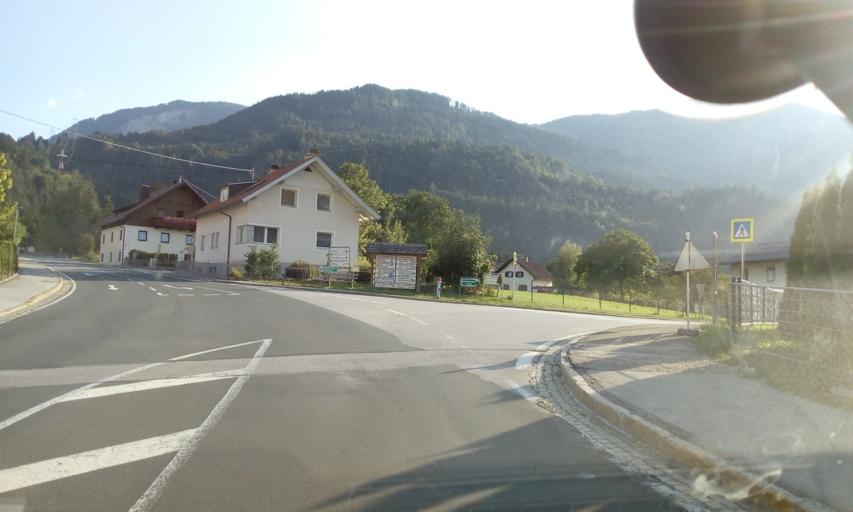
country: AT
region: Carinthia
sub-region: Politischer Bezirk Spittal an der Drau
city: Oberdrauburg
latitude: 46.7460
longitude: 12.9697
